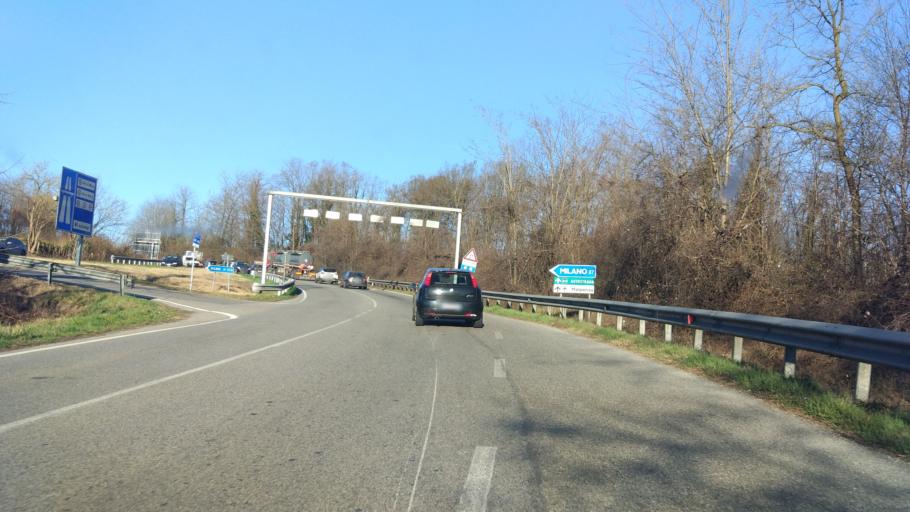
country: IT
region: Lombardy
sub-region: Provincia di Monza e Brianza
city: Briosco
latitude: 45.7167
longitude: 9.2272
